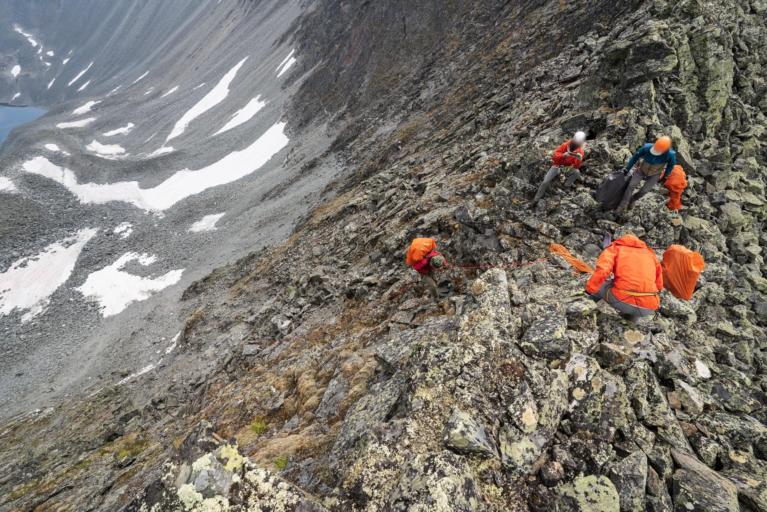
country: RU
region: Transbaikal Territory
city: Chara
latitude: 56.8337
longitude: 117.1760
